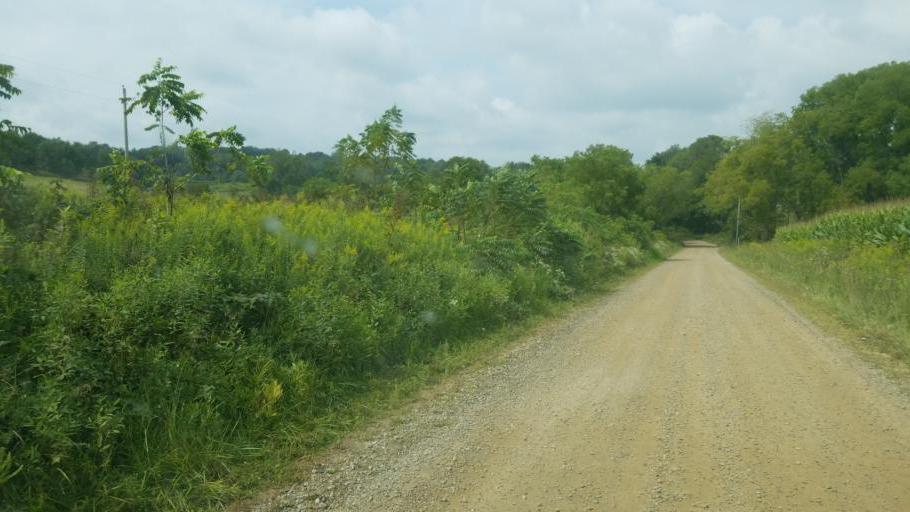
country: US
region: Ohio
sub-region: Knox County
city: Danville
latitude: 40.4783
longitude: -82.3087
